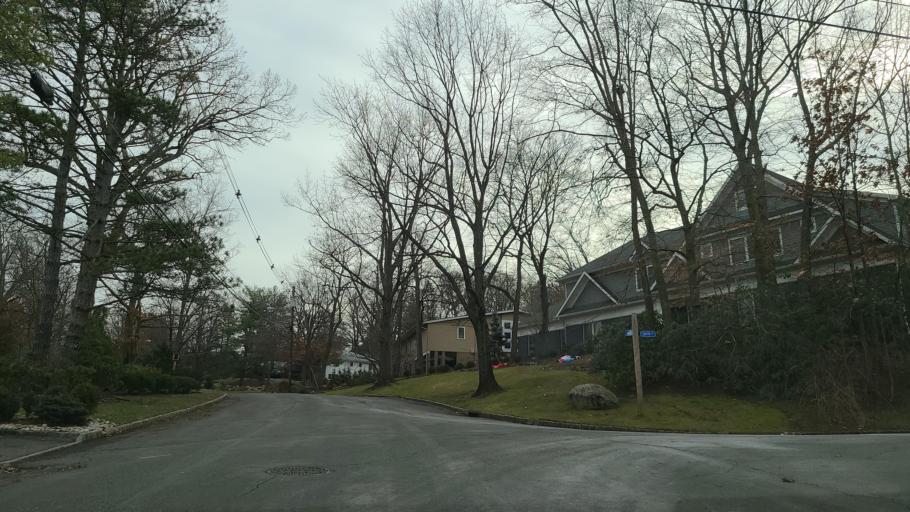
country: US
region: New Jersey
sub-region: Essex County
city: Short Hills
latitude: 40.7554
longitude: -74.3140
